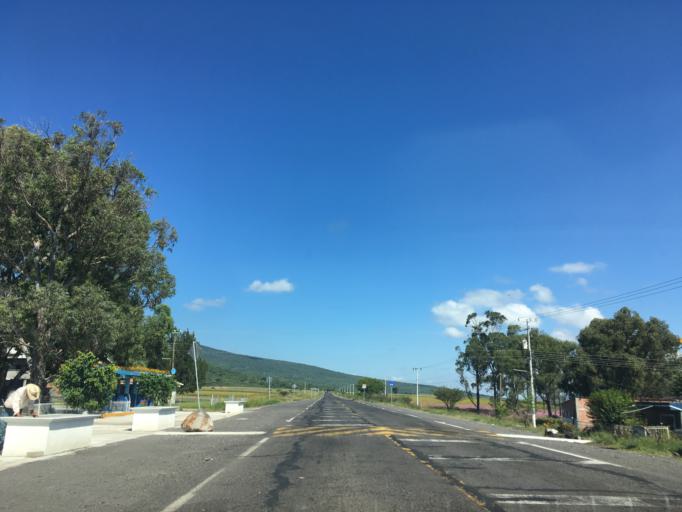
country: MX
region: Mexico
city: Tlazazalca
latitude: 20.0337
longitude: -102.0627
